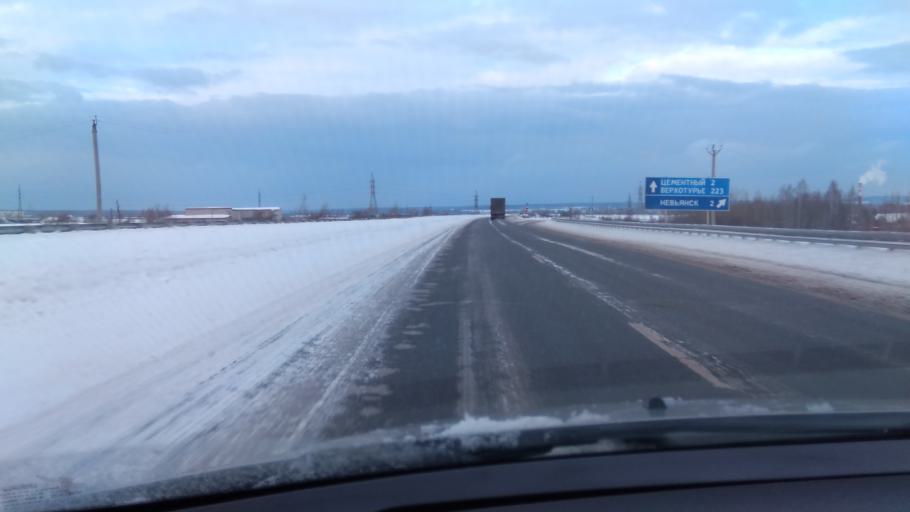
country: RU
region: Sverdlovsk
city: Tsementnyy
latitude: 57.4742
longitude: 60.1810
